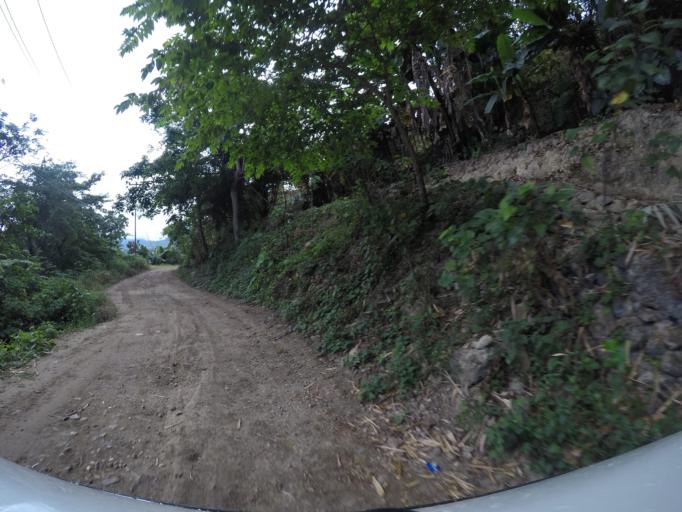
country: TL
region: Baucau
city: Baucau
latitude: -8.6431
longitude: 126.6347
